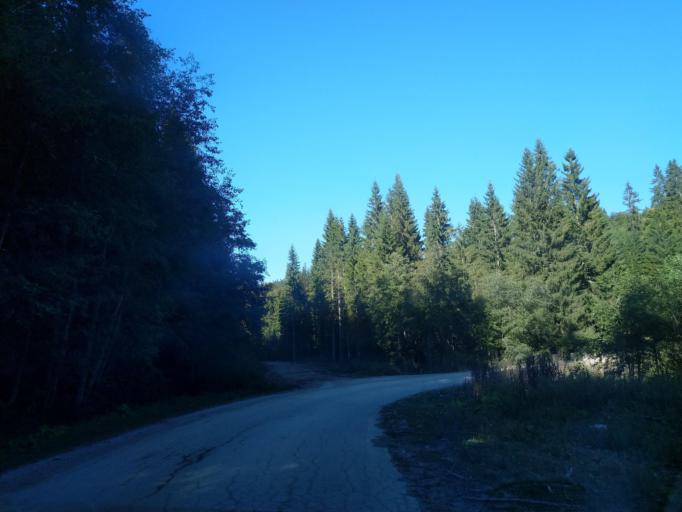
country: RS
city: Sokolovica
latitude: 43.3627
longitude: 20.2573
